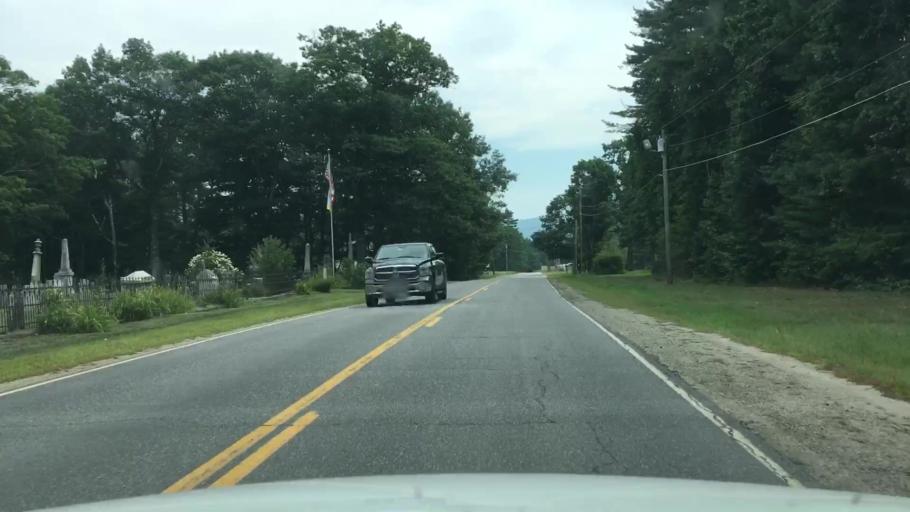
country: US
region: Maine
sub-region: Oxford County
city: Rumford
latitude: 44.6223
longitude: -70.7453
